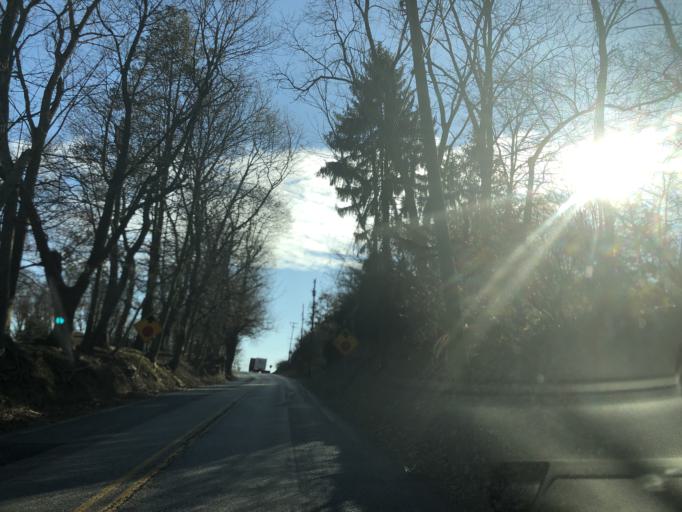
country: US
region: Pennsylvania
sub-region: Chester County
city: Upland
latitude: 39.8713
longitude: -75.7728
